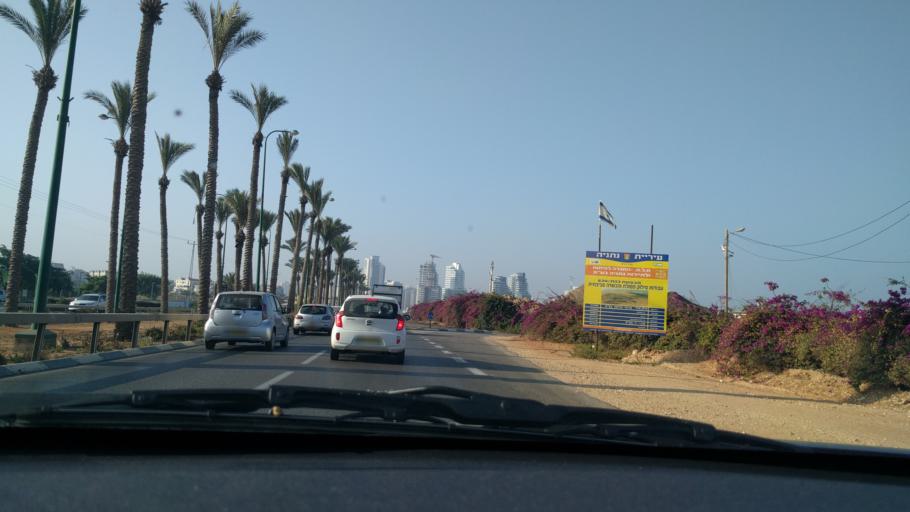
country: IL
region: Central District
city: Netanya
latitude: 32.2914
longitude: 34.8423
